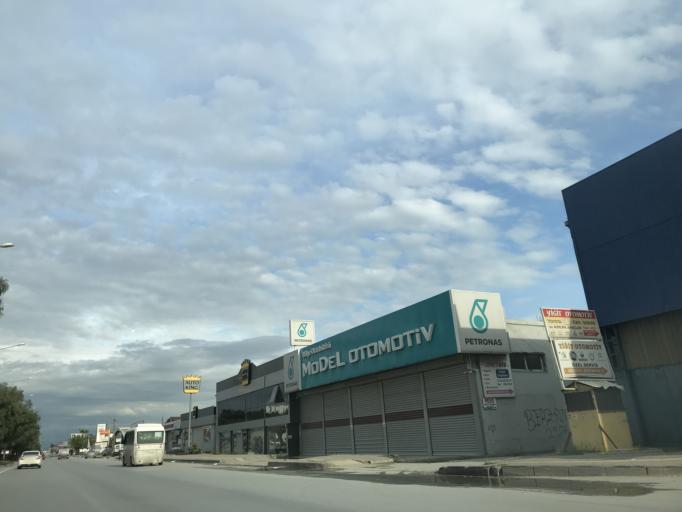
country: TR
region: Adana
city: Seyhan
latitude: 36.9955
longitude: 35.2692
